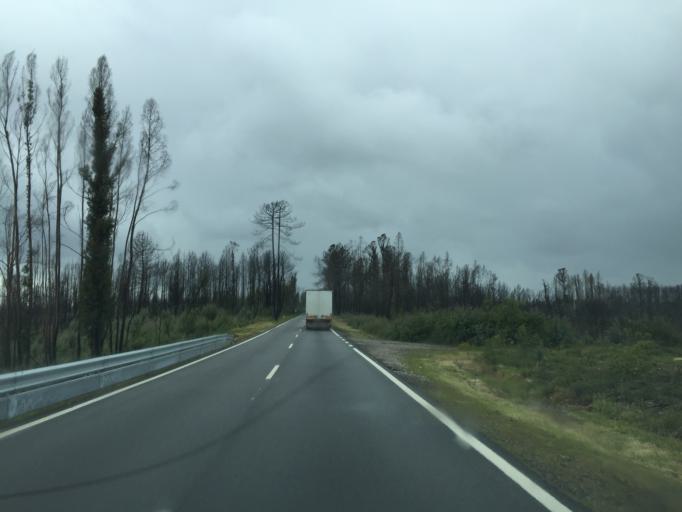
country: PT
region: Coimbra
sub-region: Oliveira do Hospital
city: Oliveira do Hospital
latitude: 40.3270
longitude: -7.9367
